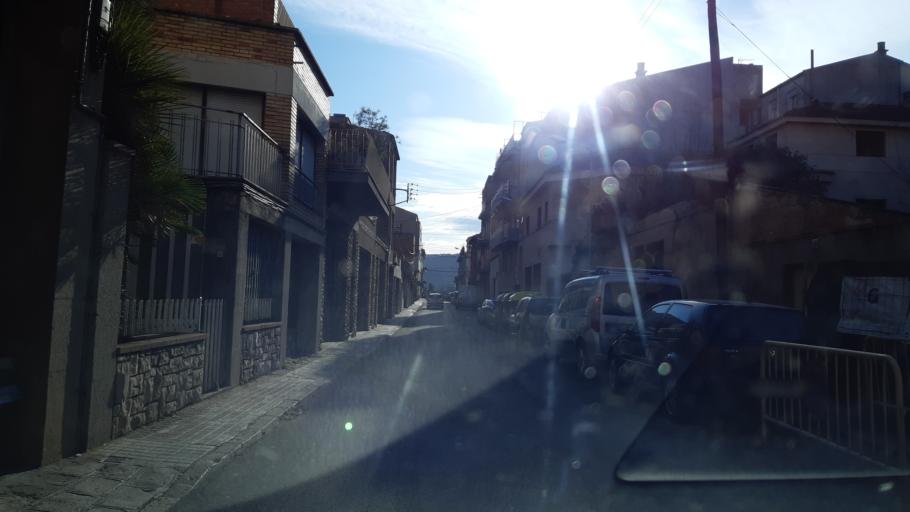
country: ES
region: Catalonia
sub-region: Provincia de Barcelona
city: Vilanova del Cami
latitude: 41.5760
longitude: 1.6305
